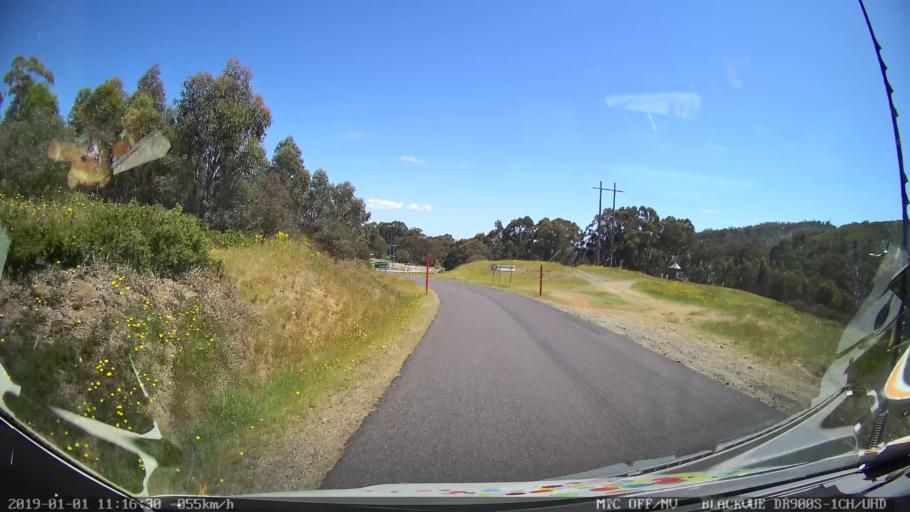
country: AU
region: New South Wales
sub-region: Snowy River
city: Jindabyne
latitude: -35.9387
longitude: 148.3856
